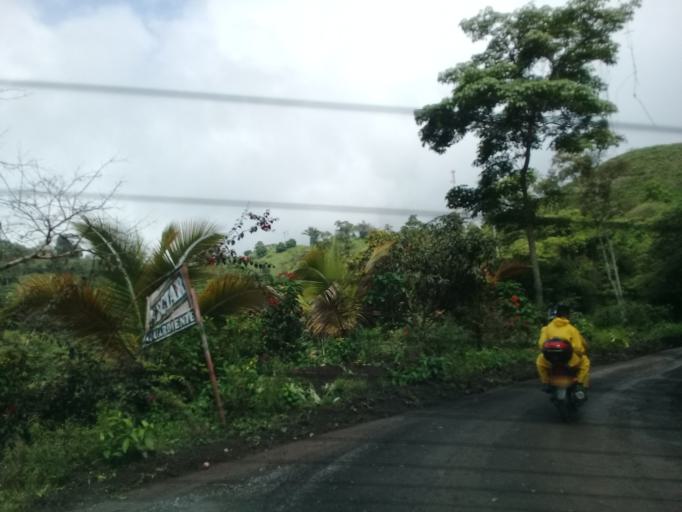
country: CO
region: Cundinamarca
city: Quipile
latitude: 4.6806
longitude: -74.5401
